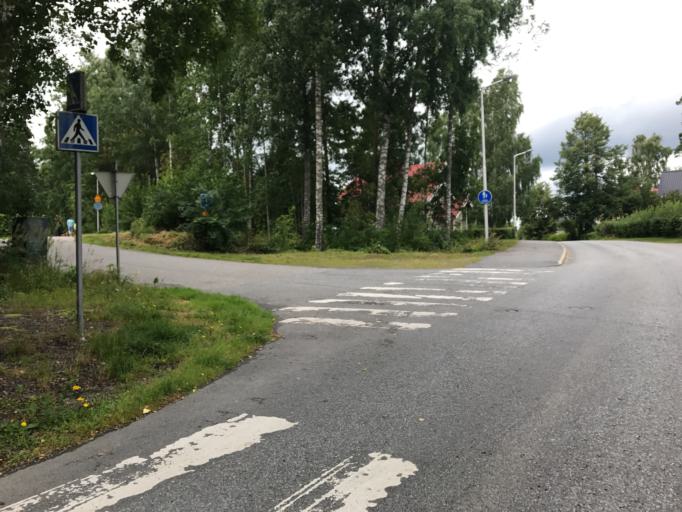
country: FI
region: Pirkanmaa
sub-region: Etelae-Pirkanmaa
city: Valkeakoski
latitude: 61.2592
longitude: 24.0433
